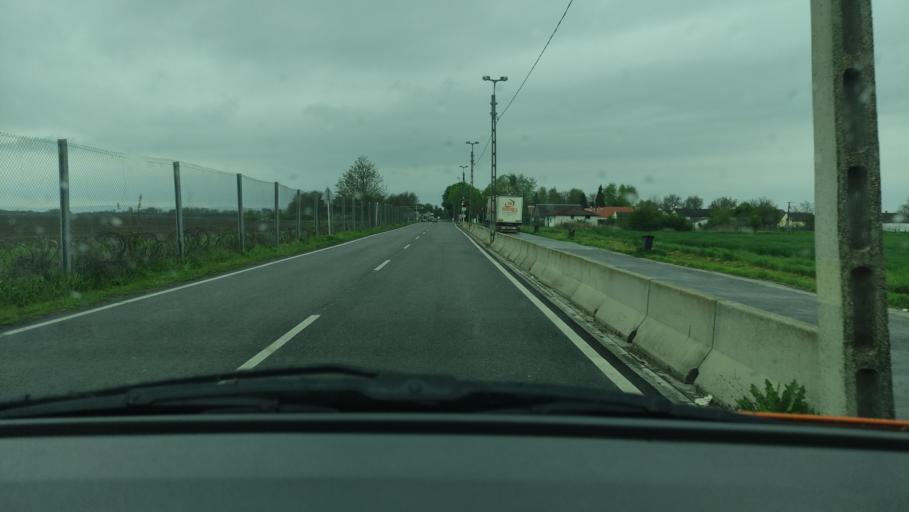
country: HU
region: Baranya
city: Mohacs
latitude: 45.9067
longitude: 18.6597
